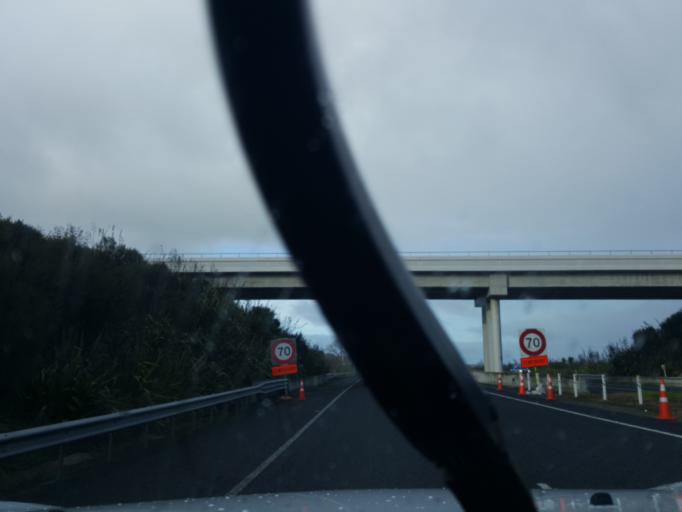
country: NZ
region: Waikato
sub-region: Waikato District
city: Ngaruawahia
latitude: -37.6325
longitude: 175.2067
